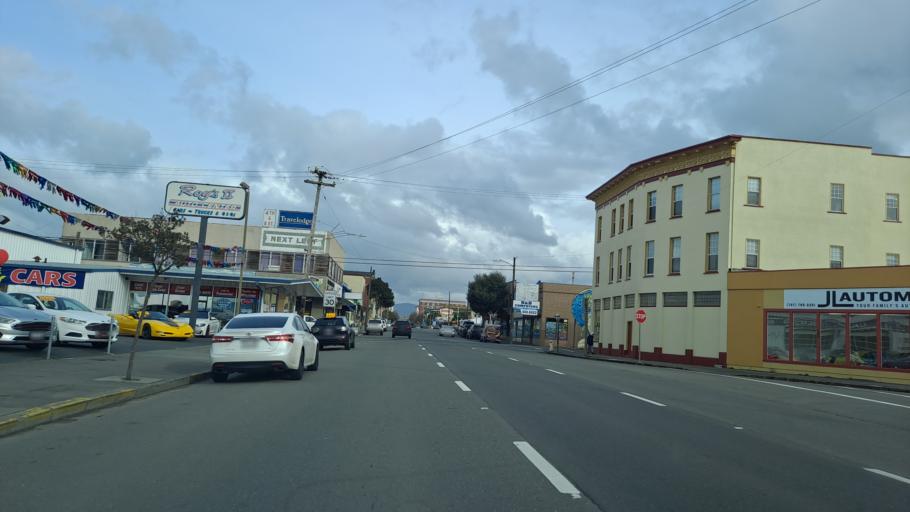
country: US
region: California
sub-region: Humboldt County
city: Eureka
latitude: 40.8011
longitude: -124.1720
